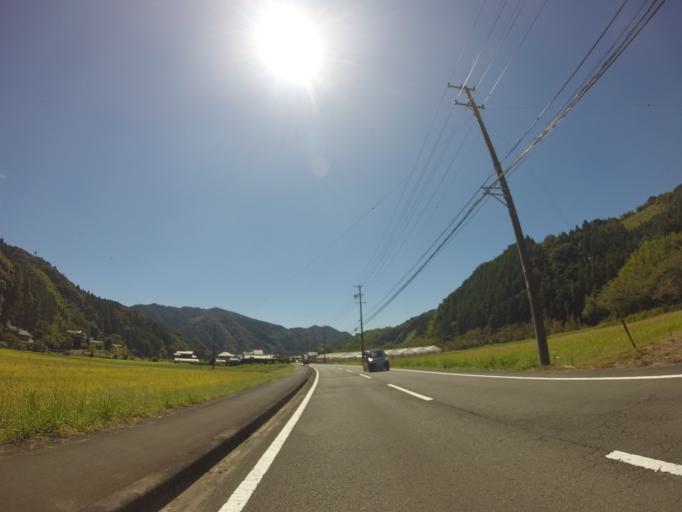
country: JP
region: Shizuoka
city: Fujieda
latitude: 34.9267
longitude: 138.2051
